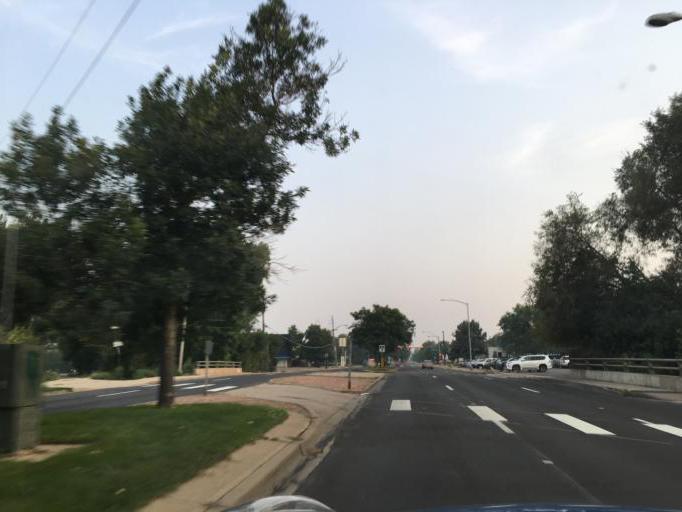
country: US
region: Colorado
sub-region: Arapahoe County
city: Glendale
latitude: 39.6697
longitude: -104.9130
